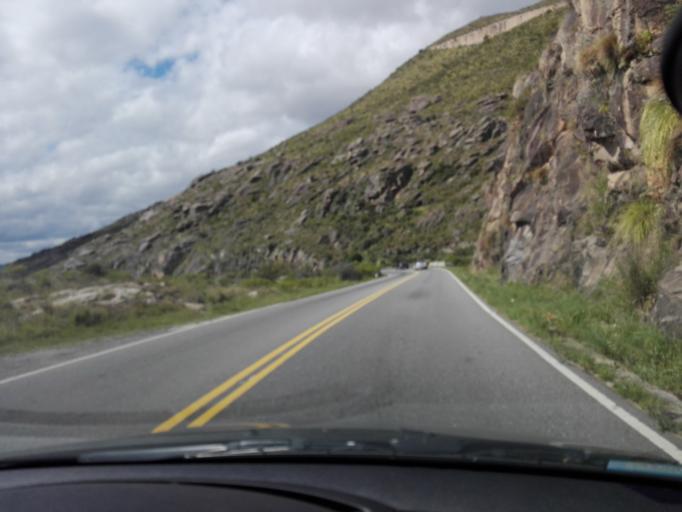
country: AR
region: Cordoba
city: Mina Clavero
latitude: -31.7720
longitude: -64.9190
